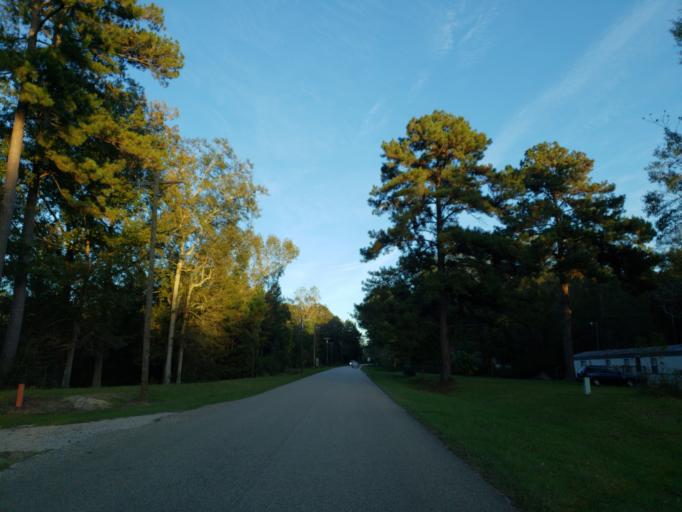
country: US
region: Mississippi
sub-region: Wayne County
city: Belmont
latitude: 31.4356
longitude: -88.4822
